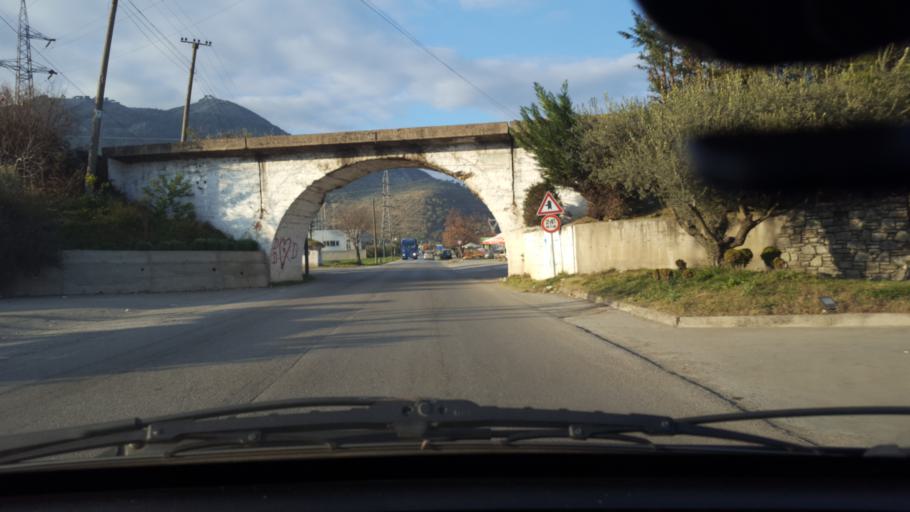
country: AL
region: Elbasan
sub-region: Rrethi i Elbasanit
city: Bradashesh
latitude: 41.1011
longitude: 20.0289
